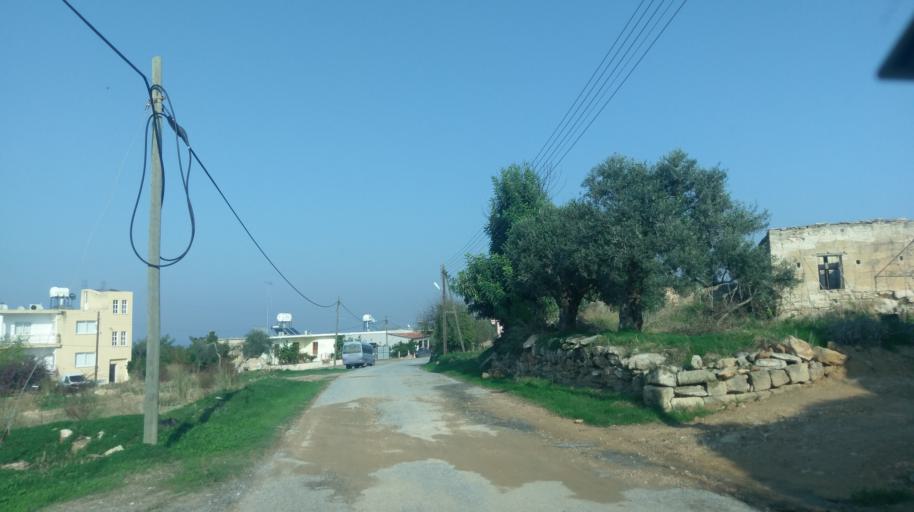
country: CY
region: Ammochostos
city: Leonarisso
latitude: 35.5409
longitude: 34.2177
